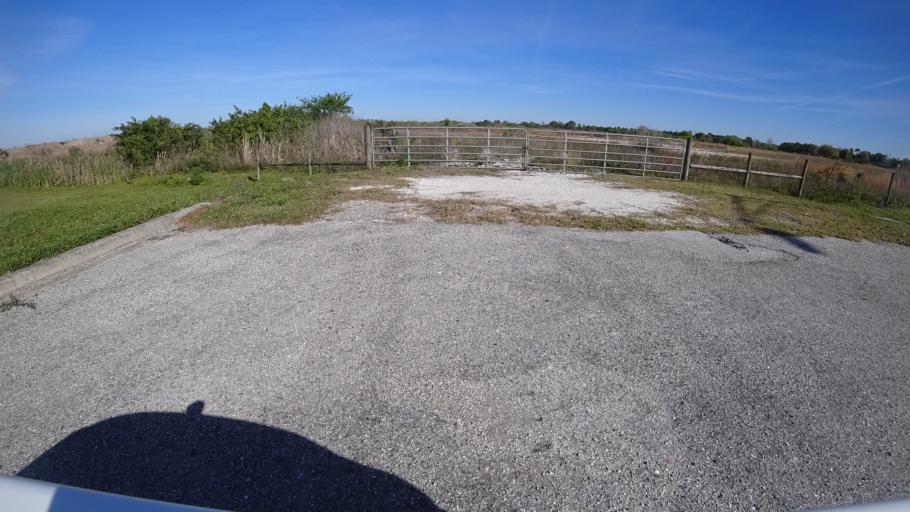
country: US
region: Florida
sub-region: Sarasota County
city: The Meadows
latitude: 27.4419
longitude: -82.4168
